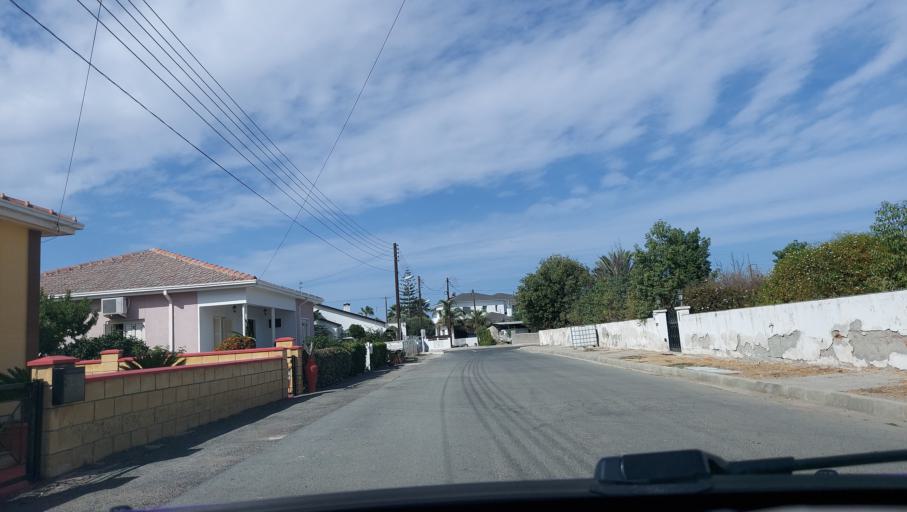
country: CY
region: Lefkosia
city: Pano Deftera
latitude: 35.0740
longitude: 33.2633
